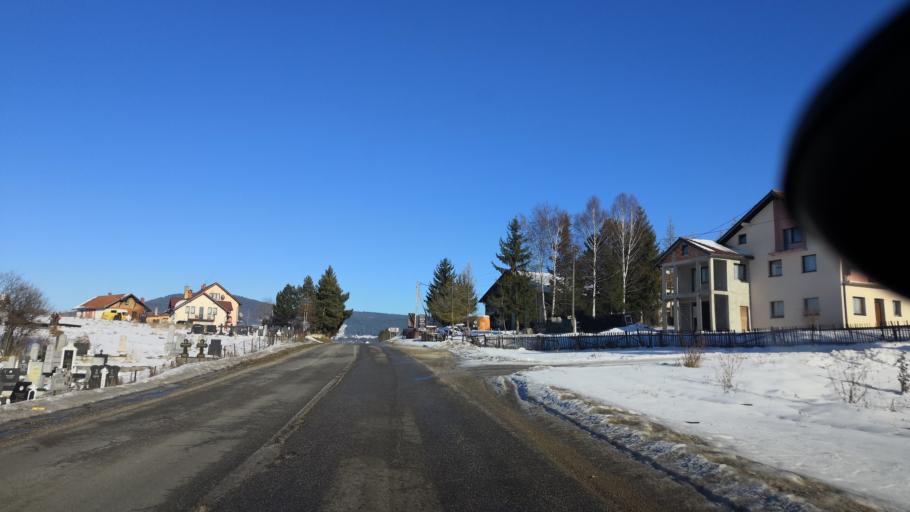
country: BA
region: Republika Srpska
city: Sokolac
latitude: 43.9490
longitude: 18.8381
